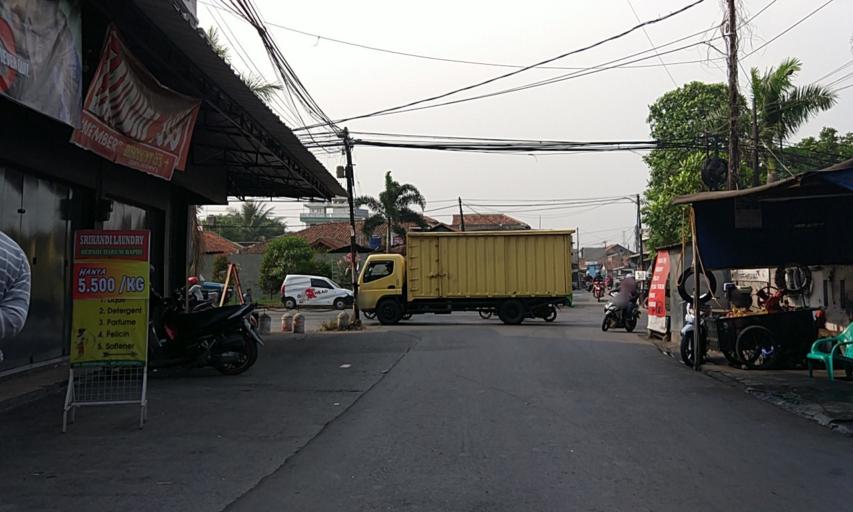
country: ID
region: West Java
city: Margahayukencana
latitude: -6.9633
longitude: 107.5612
